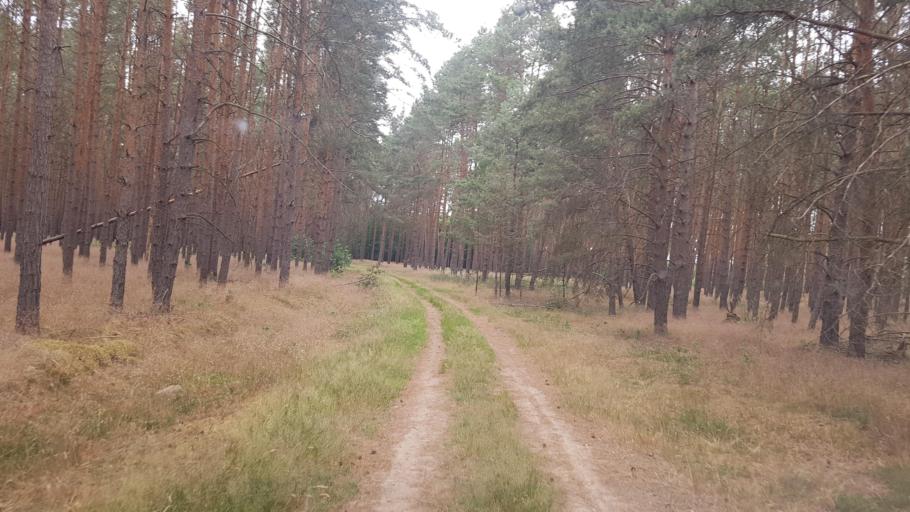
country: DE
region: Brandenburg
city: Treuenbrietzen
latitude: 52.0344
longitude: 12.8433
